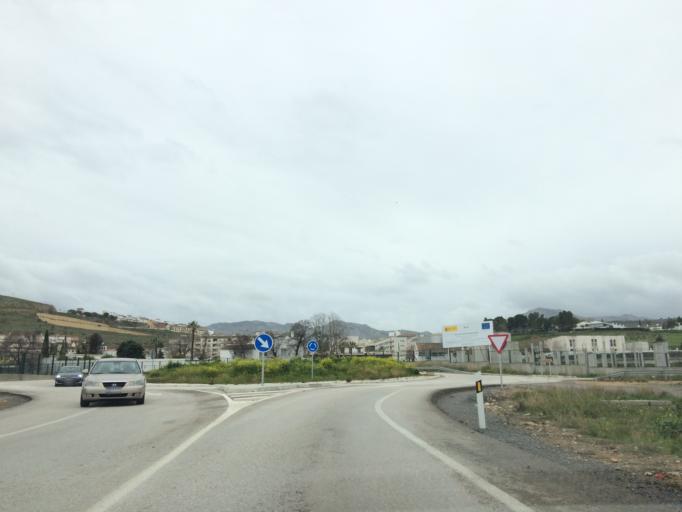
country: ES
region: Andalusia
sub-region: Provincia de Malaga
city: Antequera
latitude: 37.0307
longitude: -4.5608
